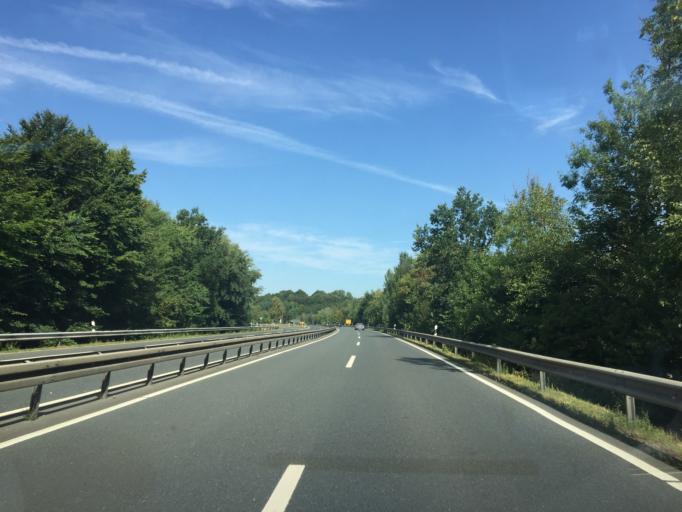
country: DE
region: Lower Saxony
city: Seesen
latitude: 51.8626
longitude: 10.1522
